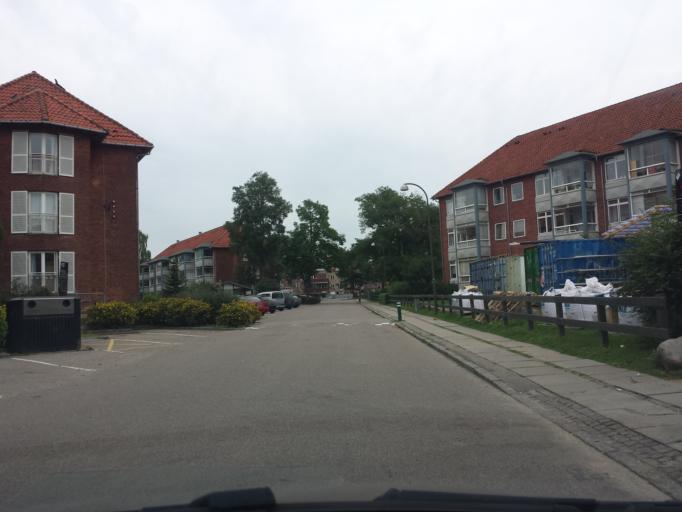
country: DK
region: Capital Region
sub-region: Herlev Kommune
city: Herlev
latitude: 55.7208
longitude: 12.4393
